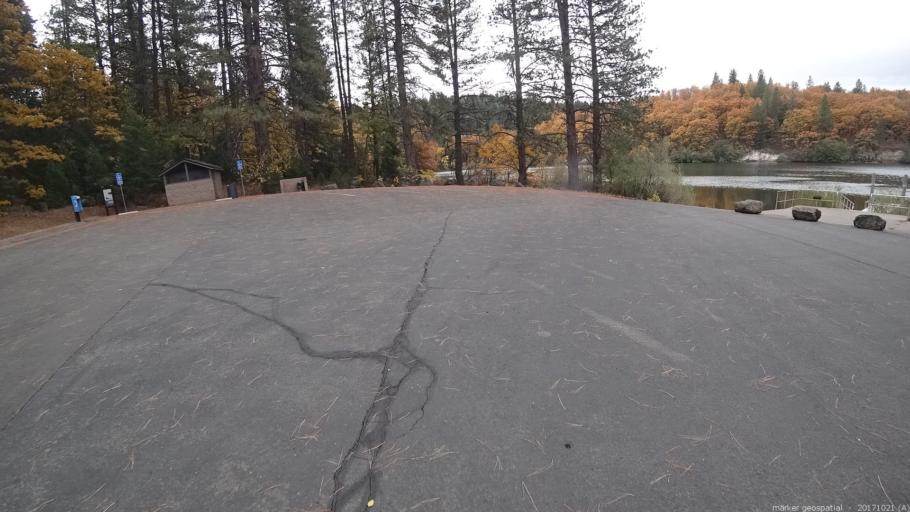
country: US
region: California
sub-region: Shasta County
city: Burney
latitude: 41.0193
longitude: -121.6229
